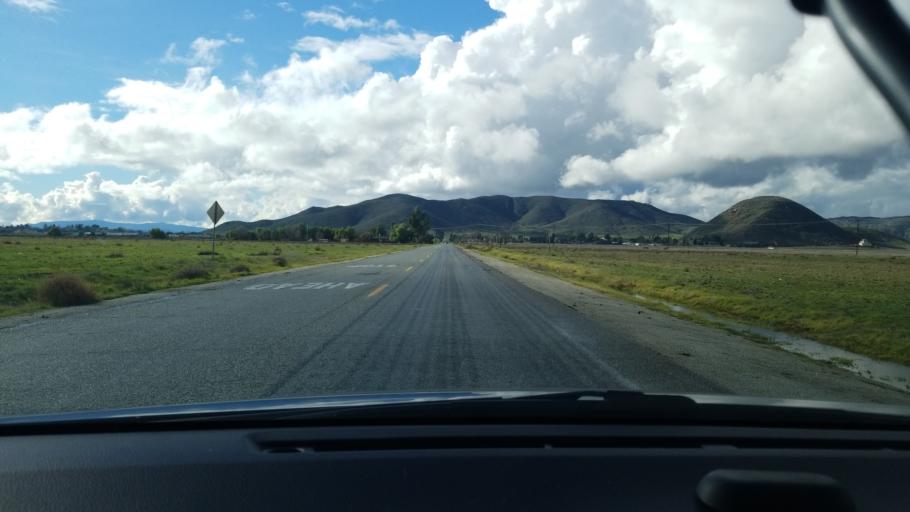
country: US
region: California
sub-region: Riverside County
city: Green Acres
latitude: 33.7292
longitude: -117.0336
